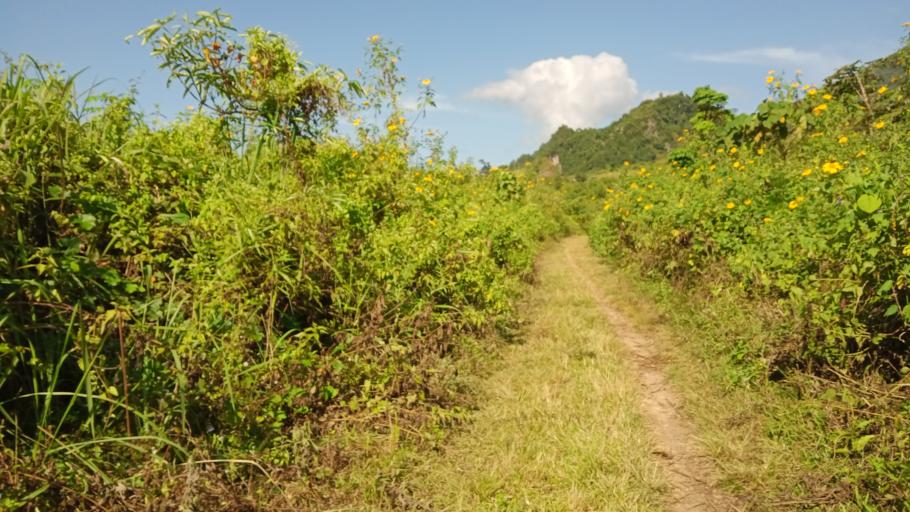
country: LA
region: Xiangkhoang
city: Phonsavan
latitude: 19.1099
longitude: 102.9302
